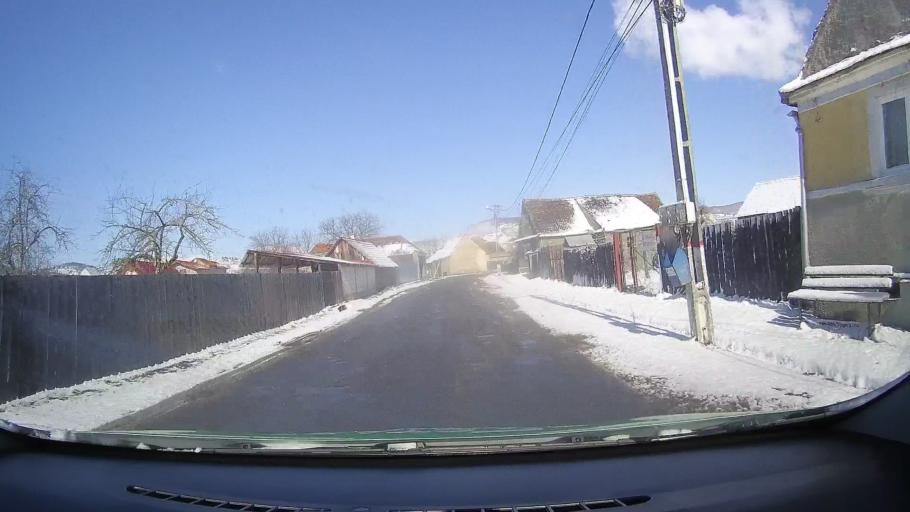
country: RO
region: Sibiu
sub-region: Comuna Avrig
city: Avrig
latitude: 45.7557
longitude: 24.3914
